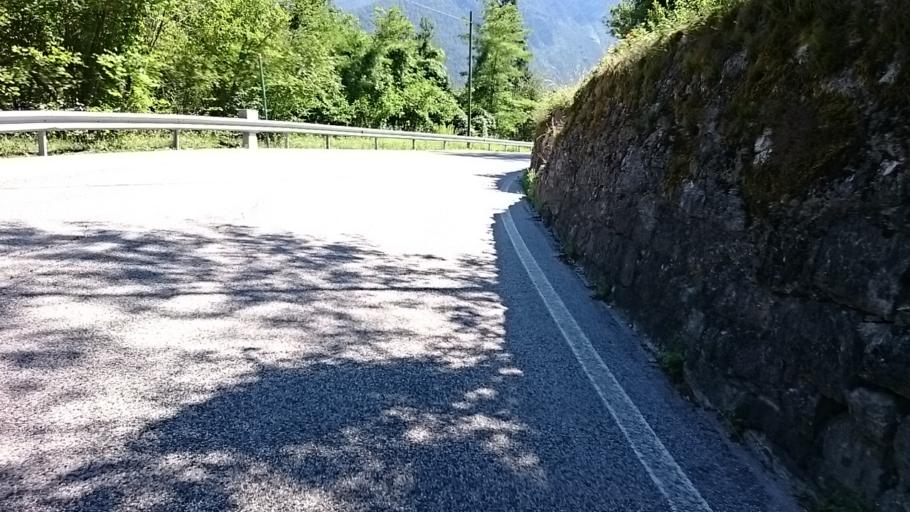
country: IT
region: Veneto
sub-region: Provincia di Belluno
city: Perarolo di Cadore
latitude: 46.3834
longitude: 12.3520
